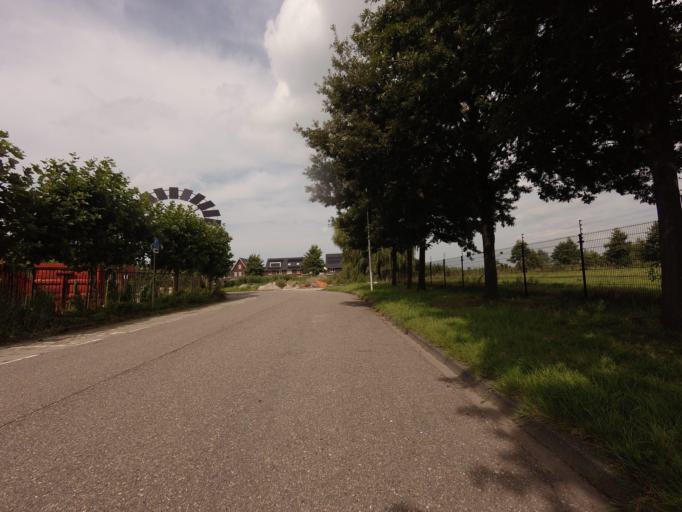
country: NL
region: South Holland
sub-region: Bodegraven-Reeuwijk
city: Bodegraven
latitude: 52.0712
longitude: 4.7652
